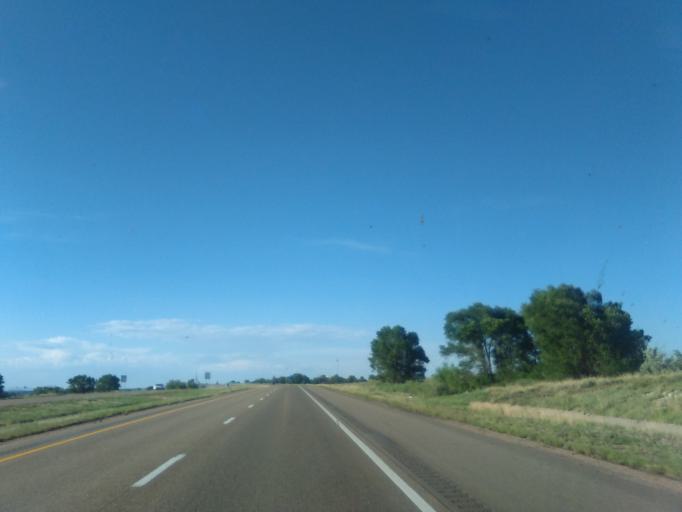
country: US
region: New Mexico
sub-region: San Miguel County
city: Las Vegas
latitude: 35.6126
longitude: -105.2039
